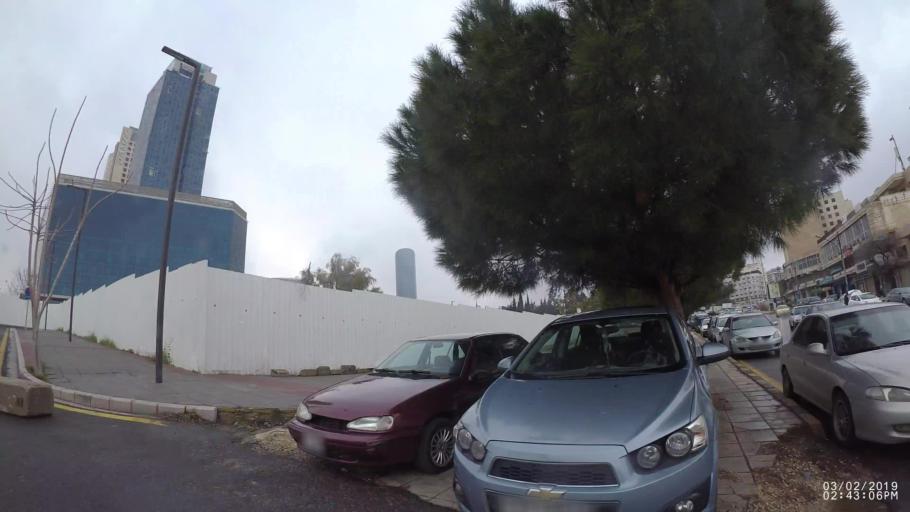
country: JO
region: Amman
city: Amman
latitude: 31.9648
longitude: 35.9116
